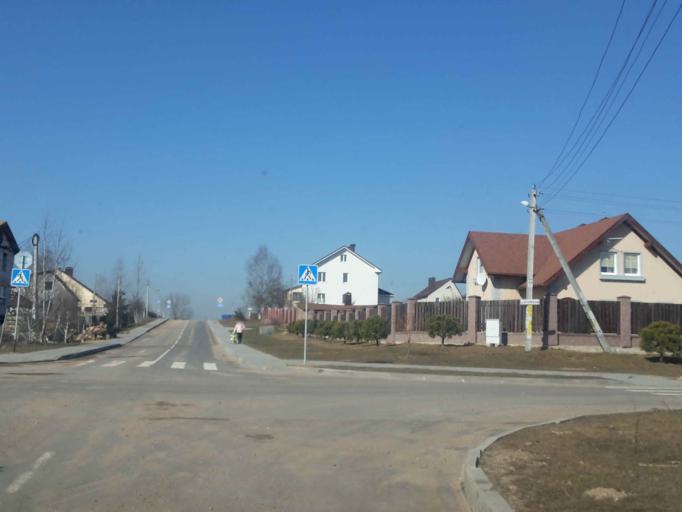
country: BY
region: Minsk
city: Zhdanovichy
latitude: 53.9234
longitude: 27.4092
